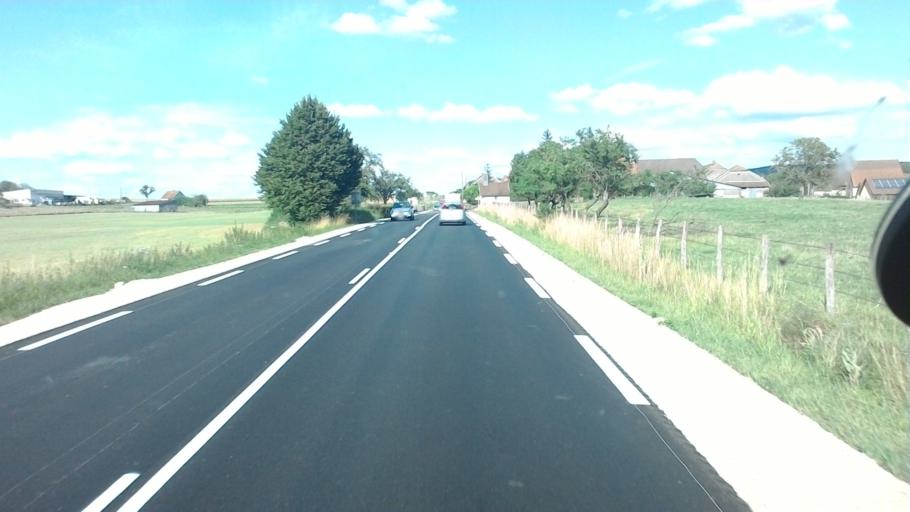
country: FR
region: Franche-Comte
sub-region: Departement de la Haute-Saone
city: Gy
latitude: 47.4295
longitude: 5.8567
